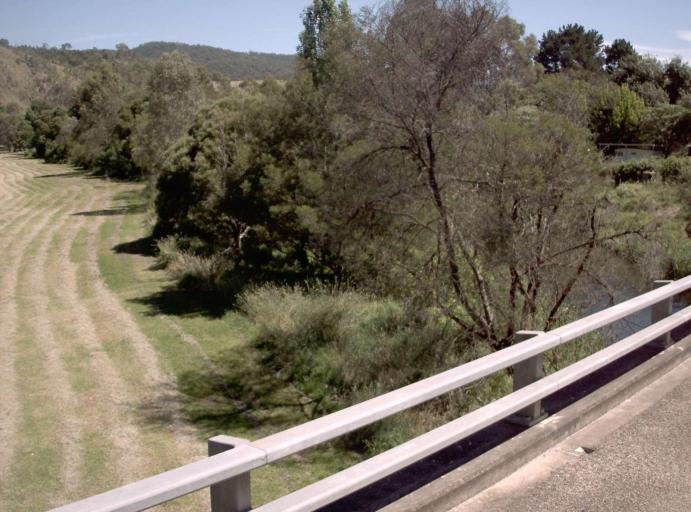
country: AU
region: Victoria
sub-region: East Gippsland
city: Lakes Entrance
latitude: -37.4967
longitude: 148.1733
